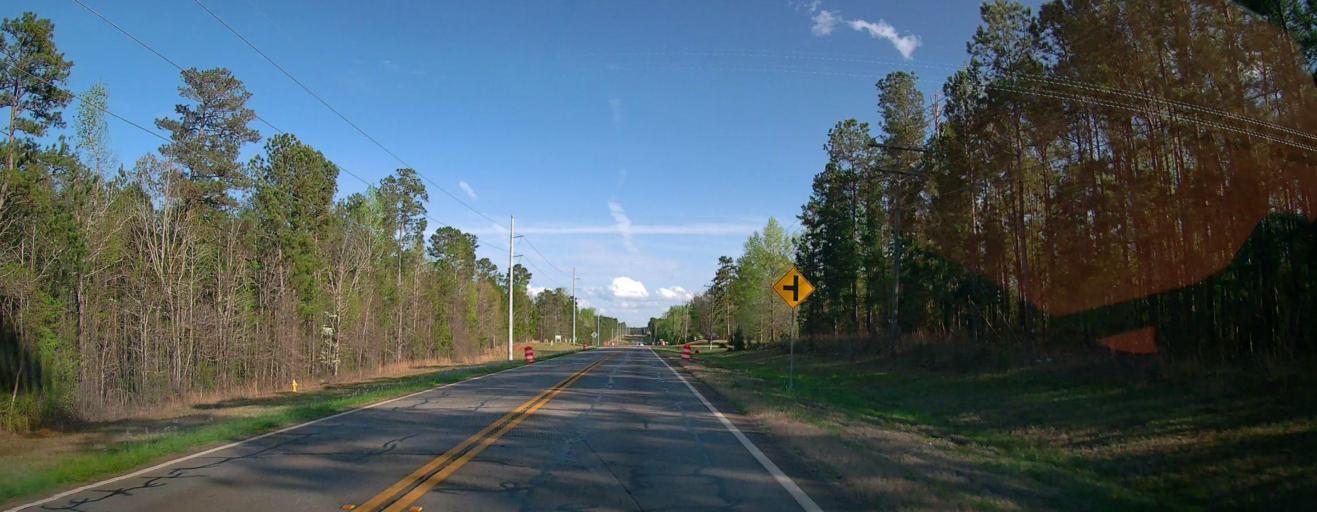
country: US
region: Georgia
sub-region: Baldwin County
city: Milledgeville
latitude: 33.1378
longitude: -83.3281
